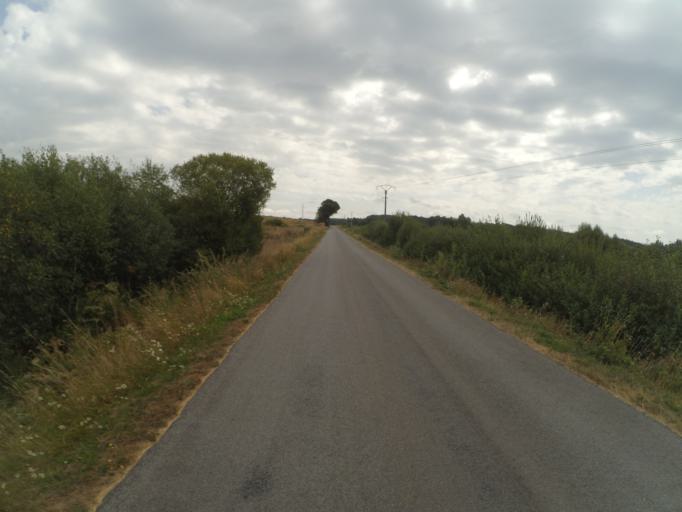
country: FR
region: Limousin
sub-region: Departement de la Creuse
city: La Courtine
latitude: 45.6649
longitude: 2.1810
